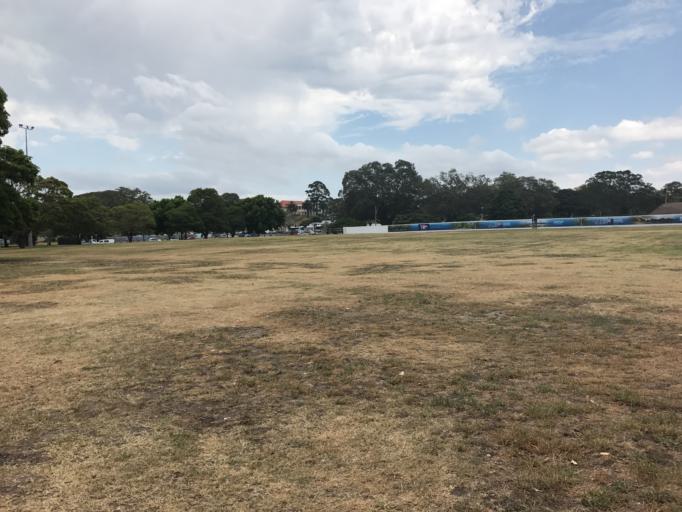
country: AU
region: New South Wales
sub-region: Woollahra
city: Paddington
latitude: -33.8939
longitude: 151.2235
